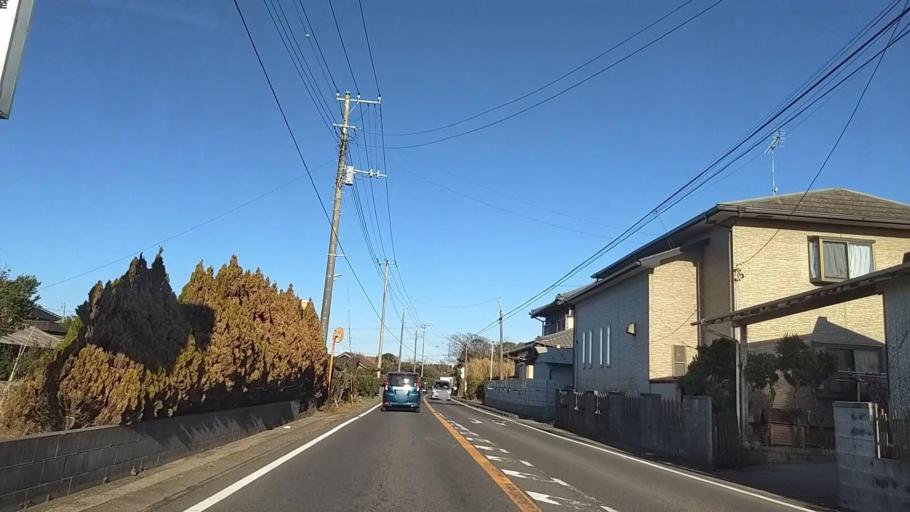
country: JP
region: Chiba
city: Yokaichiba
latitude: 35.6493
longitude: 140.5842
